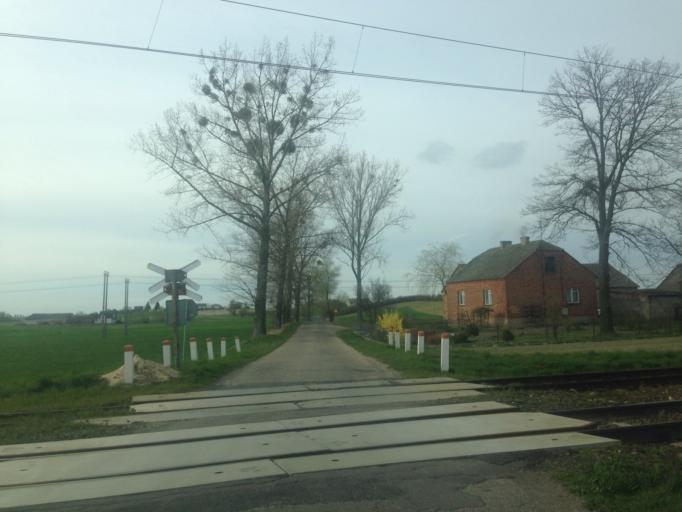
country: PL
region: Kujawsko-Pomorskie
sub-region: Powiat brodnicki
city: Jablonowo Pomorskie
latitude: 53.4059
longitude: 19.2210
